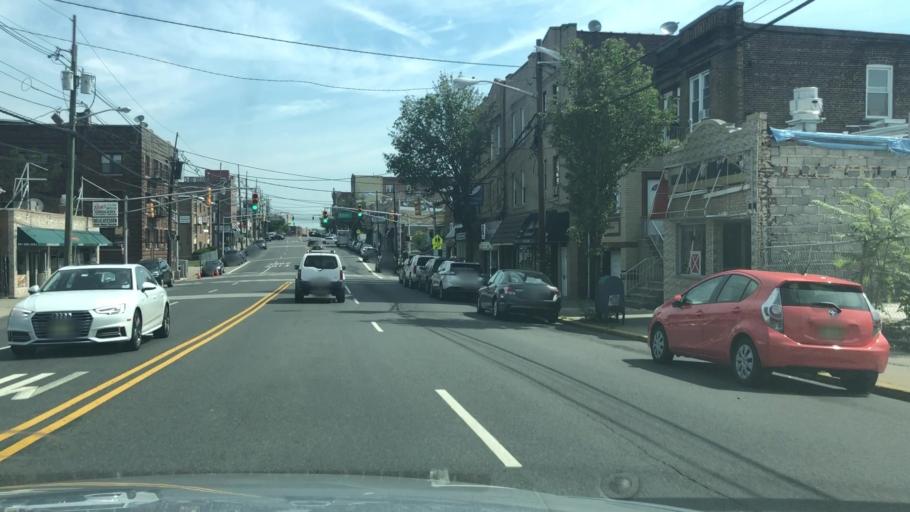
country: US
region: New Jersey
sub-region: Hudson County
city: North Bergen
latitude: 40.8057
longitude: -74.0100
